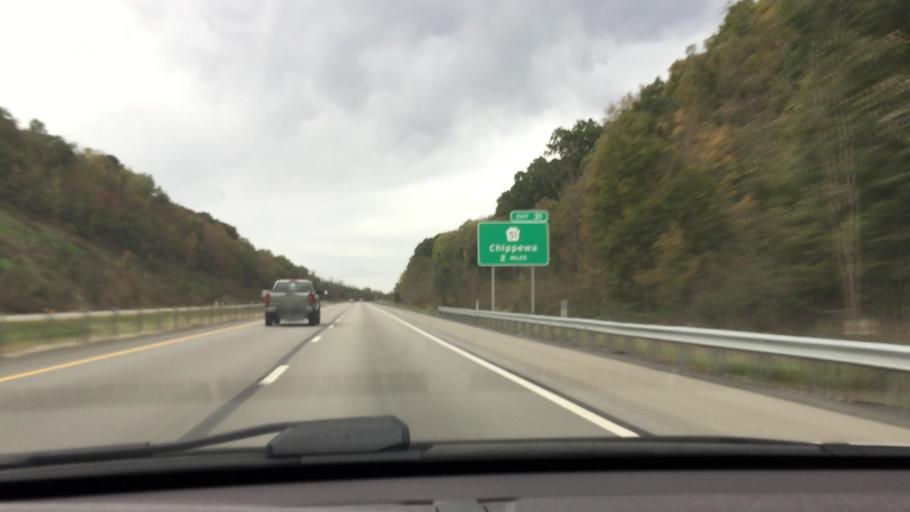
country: US
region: Pennsylvania
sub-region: Beaver County
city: Beaver Falls
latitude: 40.7283
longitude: -80.3686
